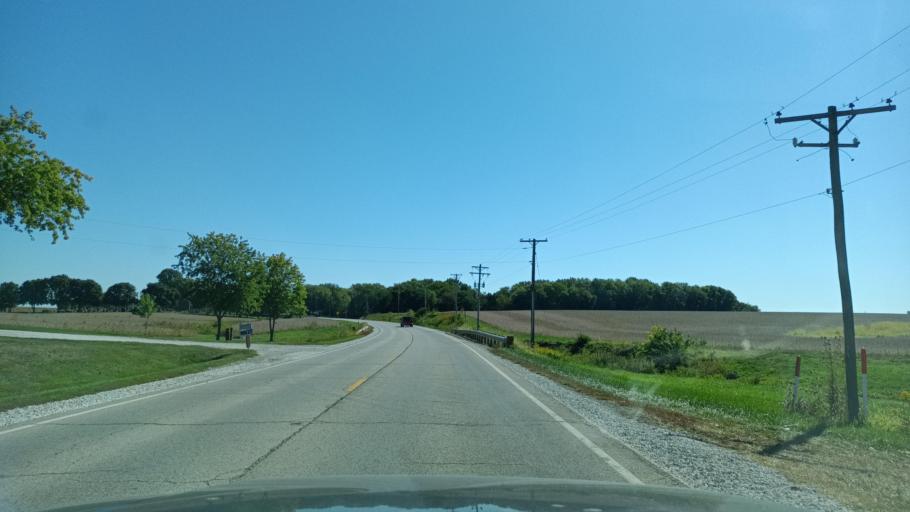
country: US
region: Illinois
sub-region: Peoria County
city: Hanna City
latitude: 40.7905
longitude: -89.7613
